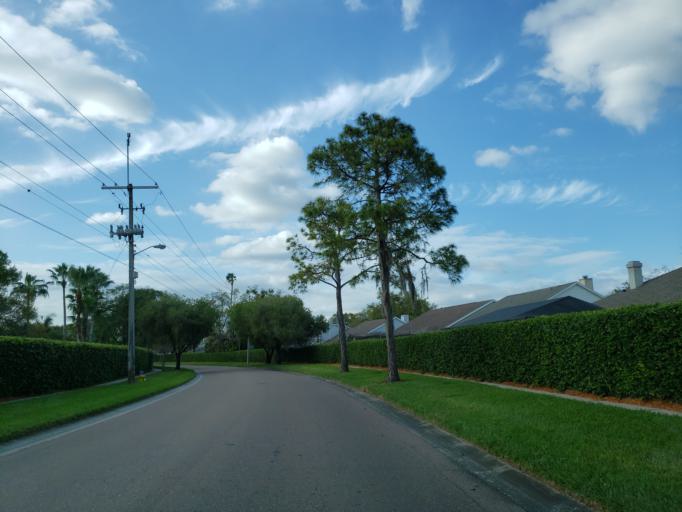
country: US
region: Florida
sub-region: Hillsborough County
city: Riverview
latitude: 27.9035
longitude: -82.3126
